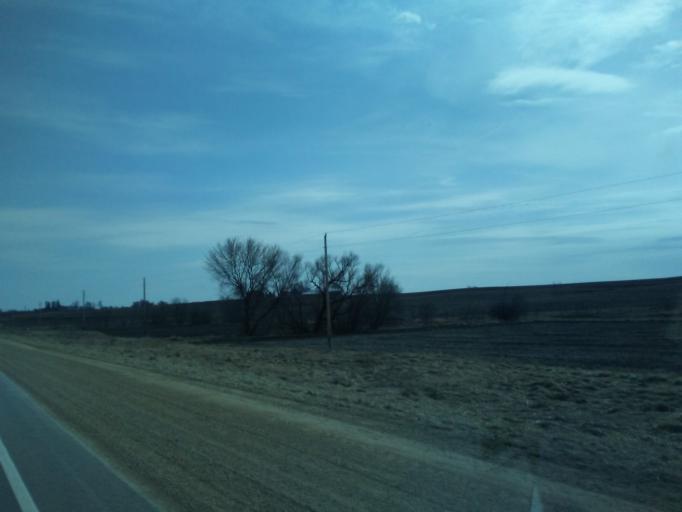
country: US
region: Iowa
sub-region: Winneshiek County
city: Decorah
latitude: 43.3929
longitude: -91.8332
